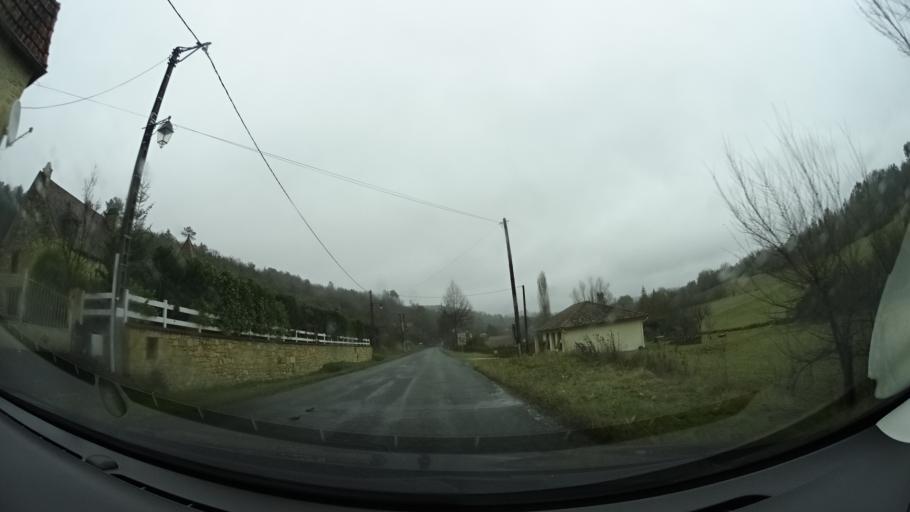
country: FR
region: Aquitaine
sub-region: Departement de la Dordogne
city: Cenac-et-Saint-Julien
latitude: 44.7293
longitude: 1.1415
